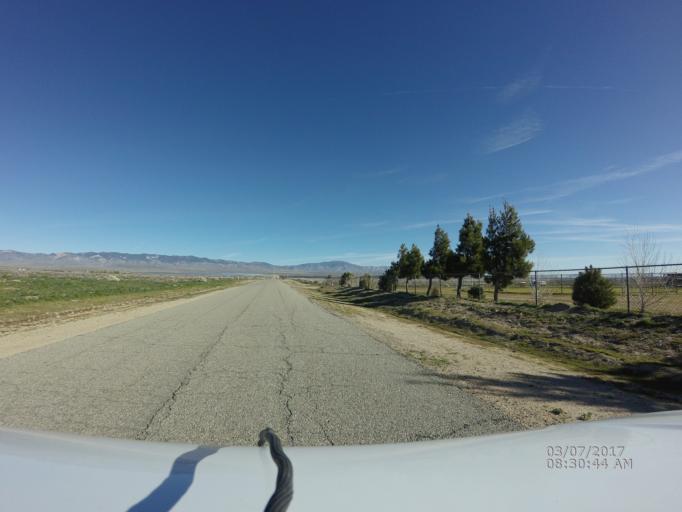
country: US
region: California
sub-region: Los Angeles County
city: Green Valley
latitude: 34.7933
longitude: -118.5369
